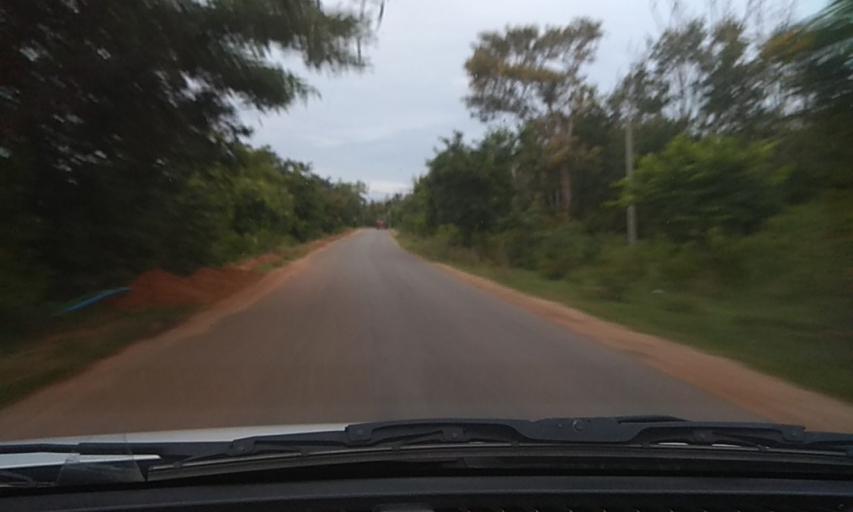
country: IN
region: Karnataka
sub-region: Chamrajnagar
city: Gundlupet
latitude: 11.7944
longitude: 76.7979
